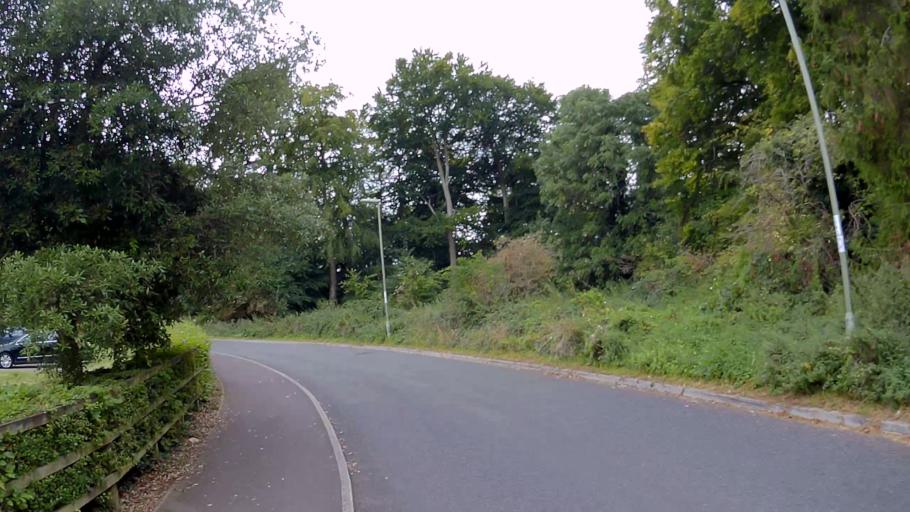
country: GB
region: England
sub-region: Hampshire
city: Basingstoke
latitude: 51.2352
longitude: -1.1200
